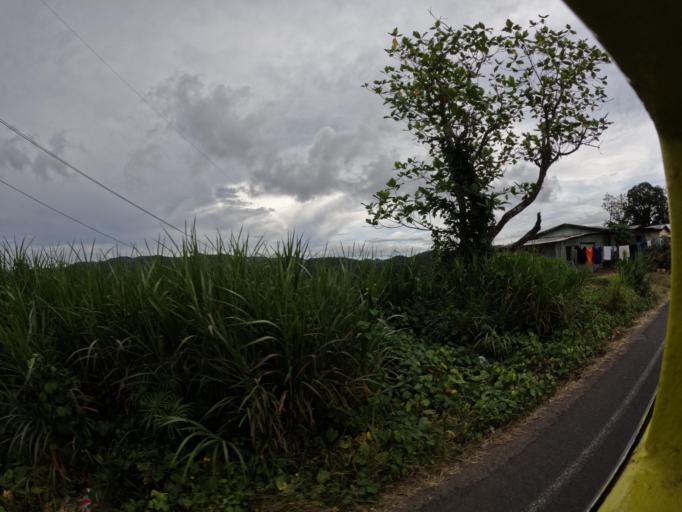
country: FJ
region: Central
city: Suva
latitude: -18.0854
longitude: 178.4516
